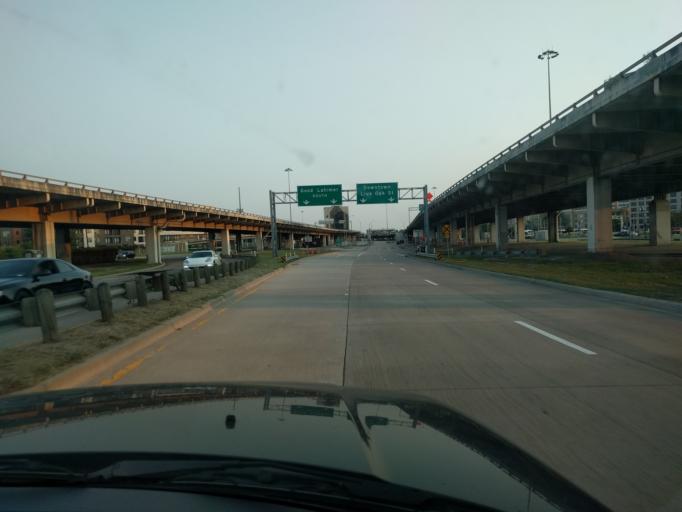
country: US
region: Texas
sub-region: Dallas County
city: Dallas
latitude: 32.7905
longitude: -96.7923
